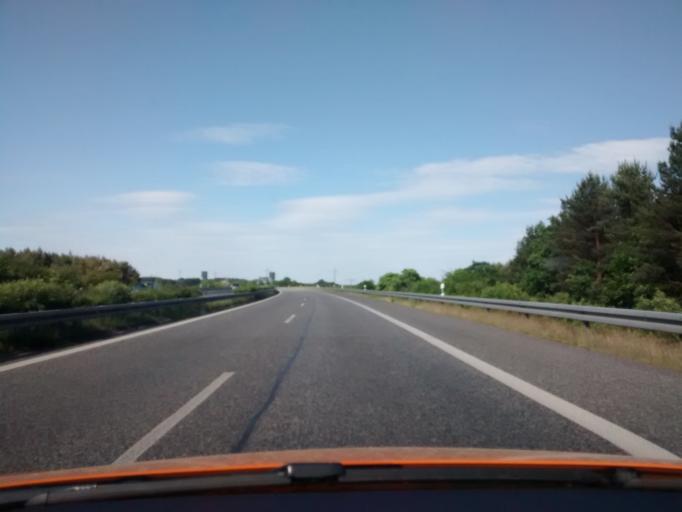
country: DE
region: Brandenburg
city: Ludwigsfelde
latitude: 52.2629
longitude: 13.2635
